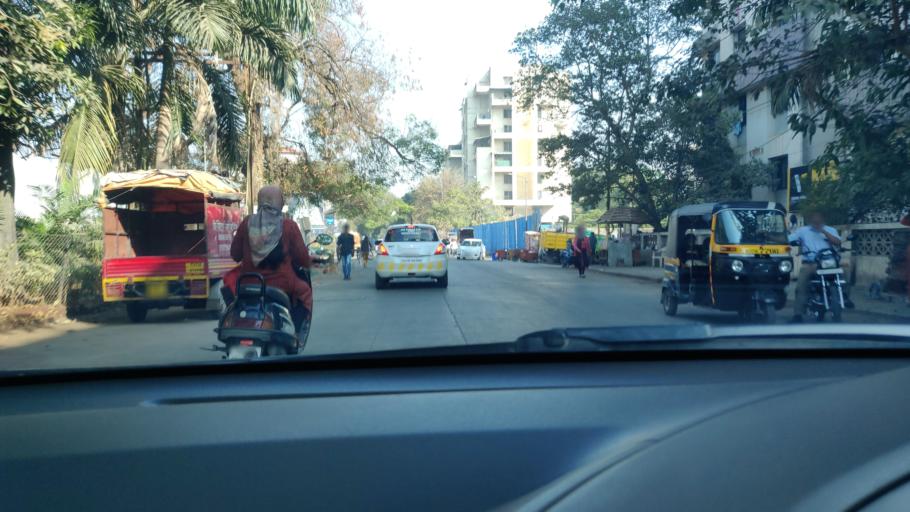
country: IN
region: Maharashtra
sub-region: Pune Division
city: Khadki
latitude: 18.5624
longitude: 73.8028
